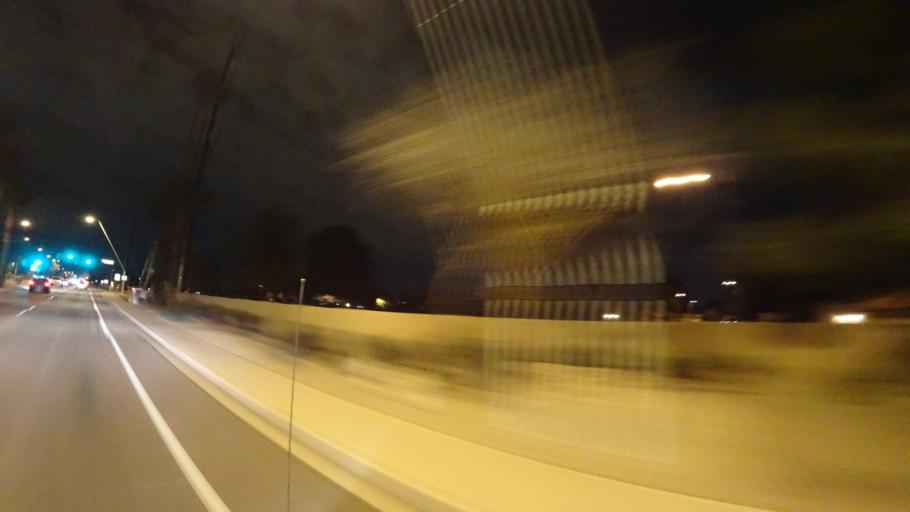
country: US
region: Arizona
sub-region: Maricopa County
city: San Carlos
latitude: 33.3563
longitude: -111.8591
